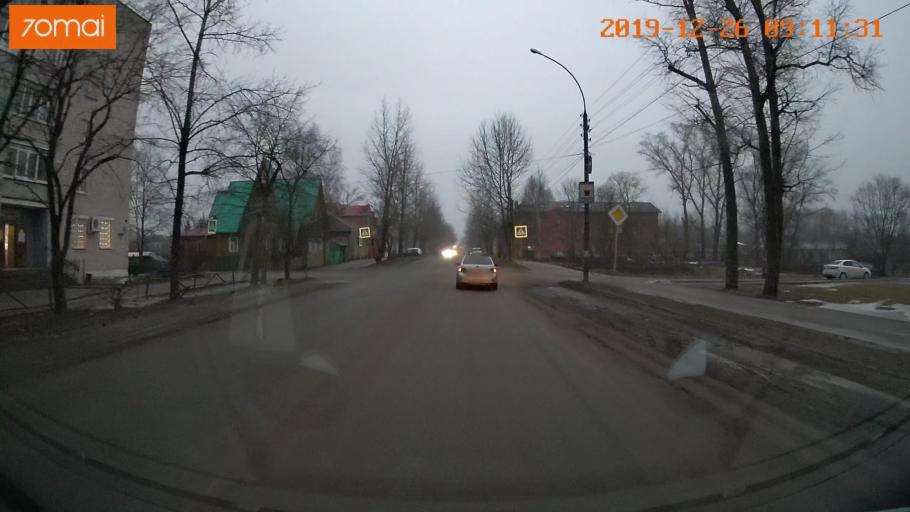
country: RU
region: Vologda
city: Gryazovets
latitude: 58.8766
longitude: 40.2527
